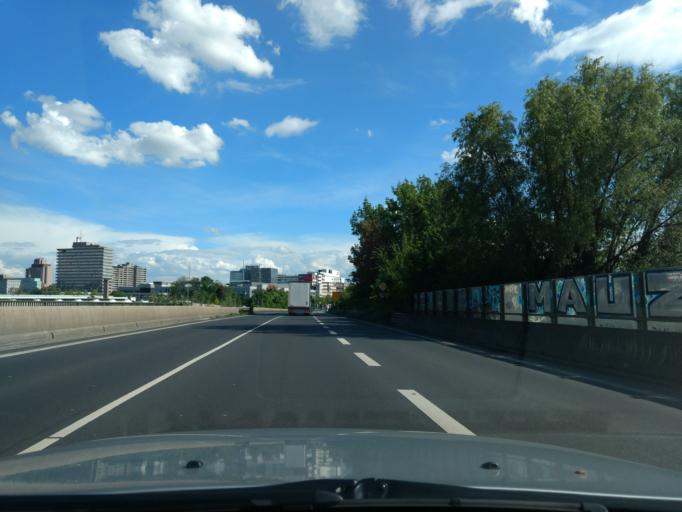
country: DE
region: North Rhine-Westphalia
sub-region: Regierungsbezirk Dusseldorf
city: Neuss
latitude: 51.2060
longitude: 6.7140
